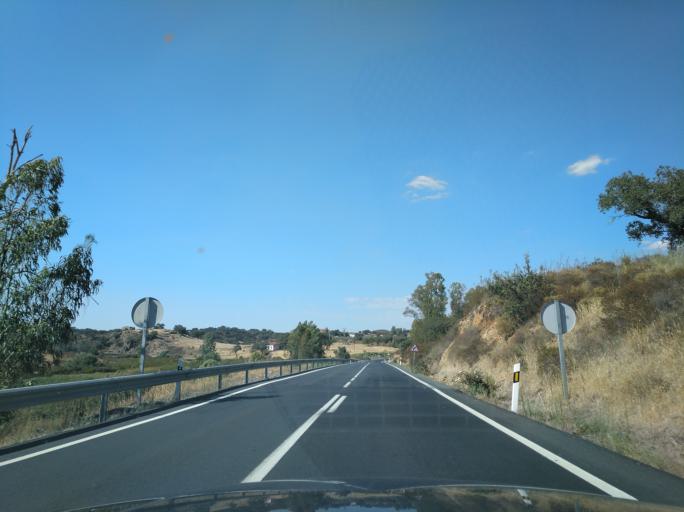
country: ES
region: Andalusia
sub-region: Provincia de Huelva
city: Alosno
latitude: 37.5321
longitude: -7.1328
